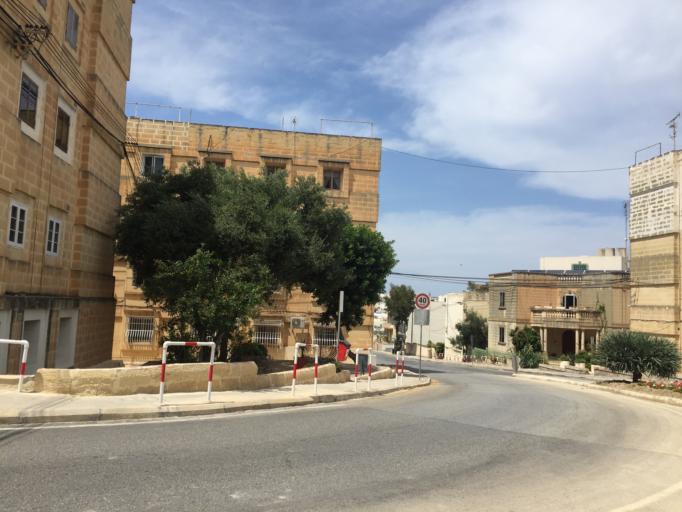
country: MT
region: Ta' Xbiex
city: Ta' Xbiex
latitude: 35.8991
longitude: 14.4945
